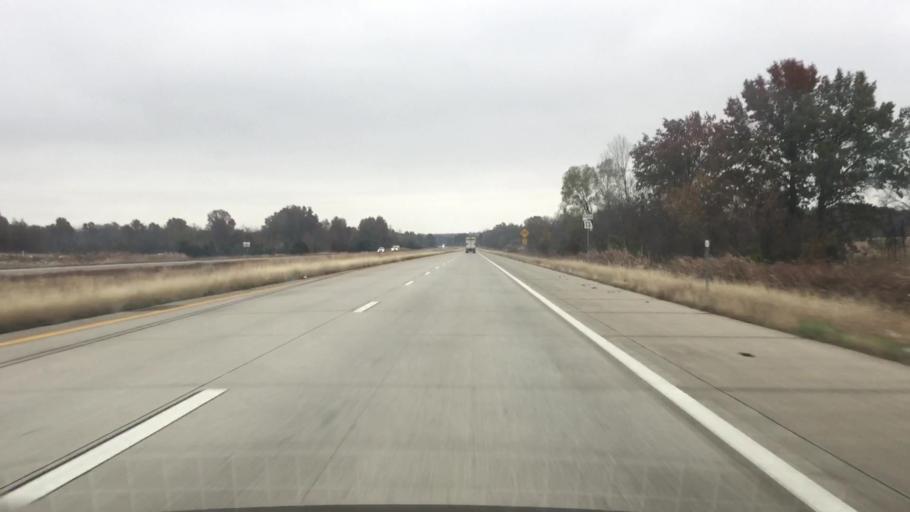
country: US
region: Missouri
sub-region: Henry County
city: Clinton
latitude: 38.2436
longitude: -93.7623
